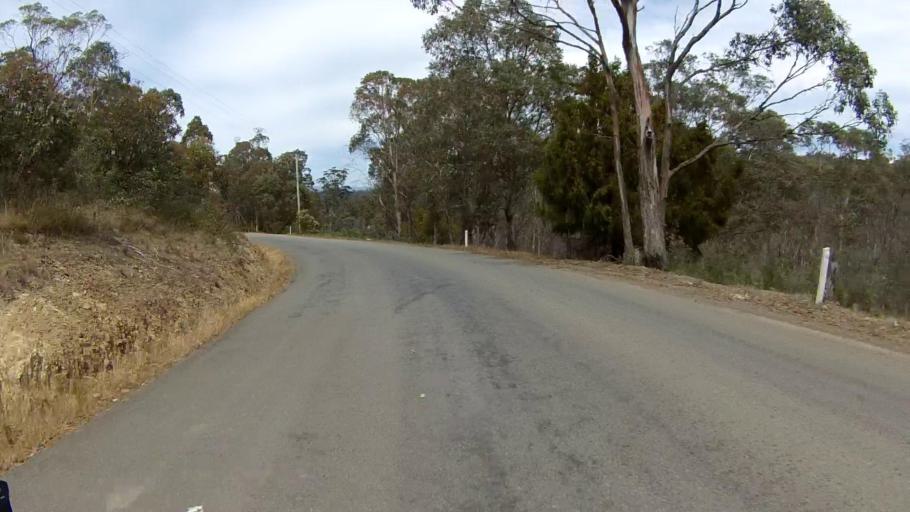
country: AU
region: Tasmania
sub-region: Sorell
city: Sorell
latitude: -42.7943
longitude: 147.6888
